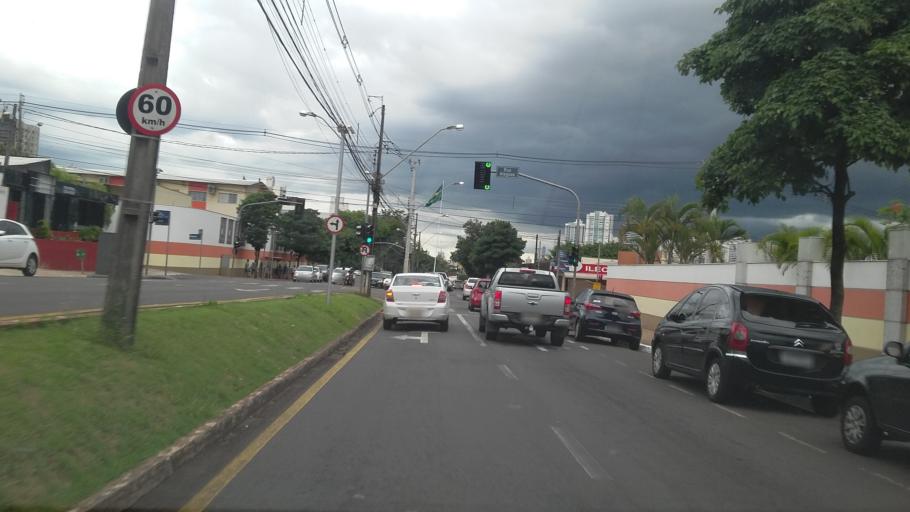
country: BR
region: Parana
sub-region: Londrina
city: Londrina
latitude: -23.3171
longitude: -51.1706
